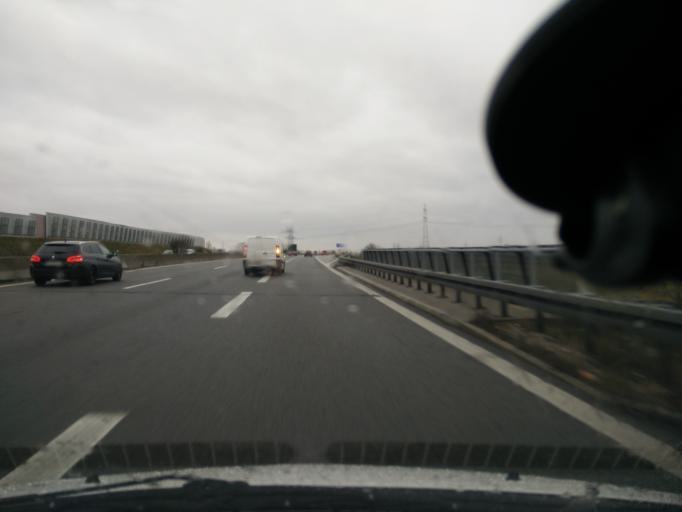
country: DE
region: Bavaria
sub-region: Upper Bavaria
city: Karlsfeld
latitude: 48.1850
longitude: 11.4354
